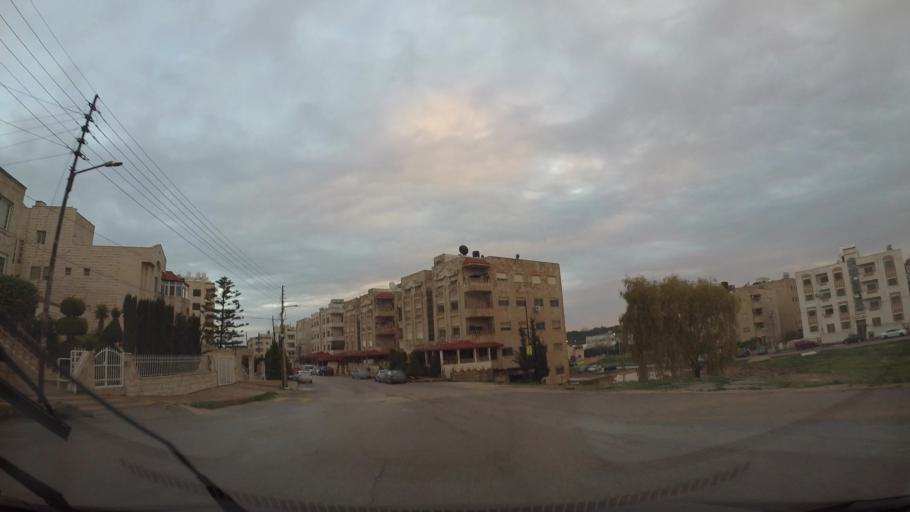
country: JO
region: Amman
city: Amman
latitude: 31.9887
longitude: 35.9119
